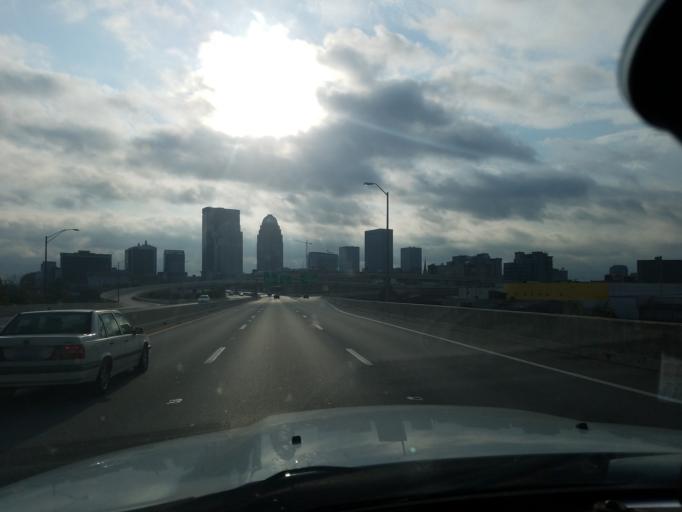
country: US
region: Kentucky
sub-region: Jefferson County
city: Louisville
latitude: 38.2600
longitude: -85.7678
